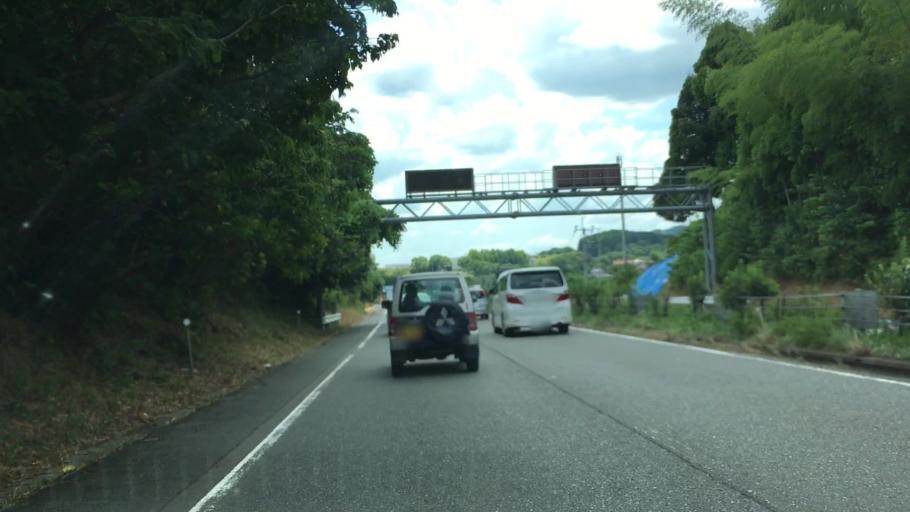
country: JP
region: Fukuoka
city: Chikushino-shi
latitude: 33.4371
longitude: 130.5252
